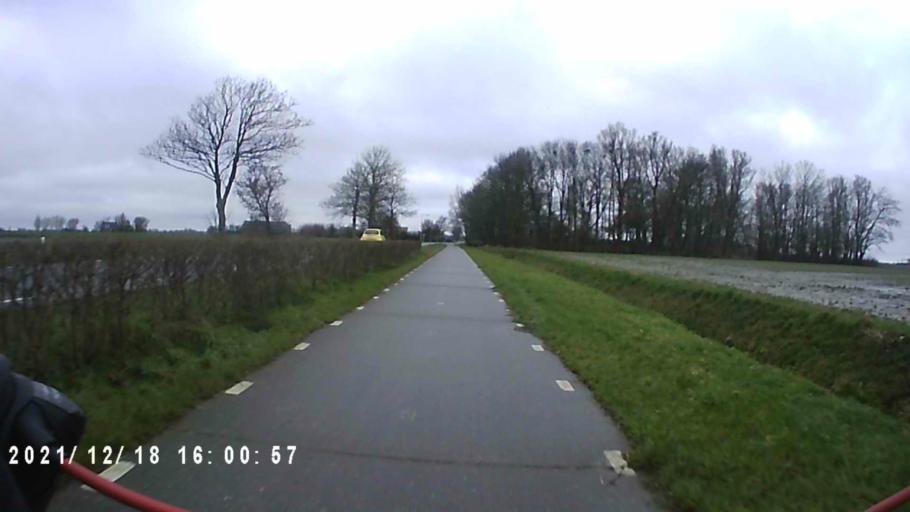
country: NL
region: Friesland
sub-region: Gemeente Dongeradeel
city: Anjum
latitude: 53.3435
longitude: 6.0870
